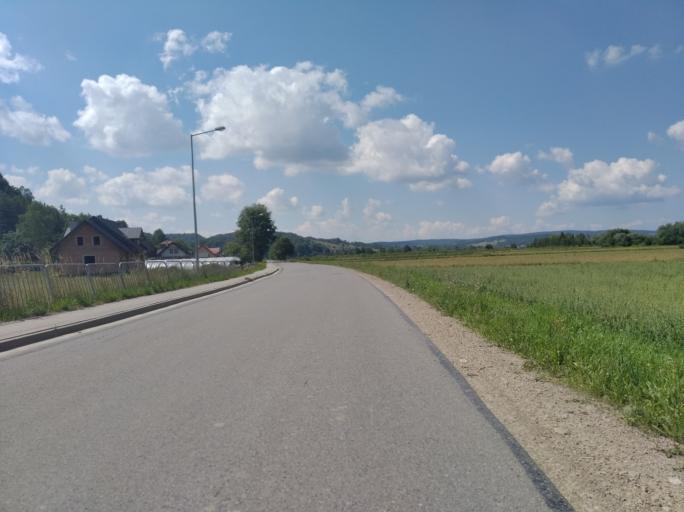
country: PL
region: Subcarpathian Voivodeship
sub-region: Powiat rzeszowski
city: Dynow
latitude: 49.7927
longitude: 22.2413
